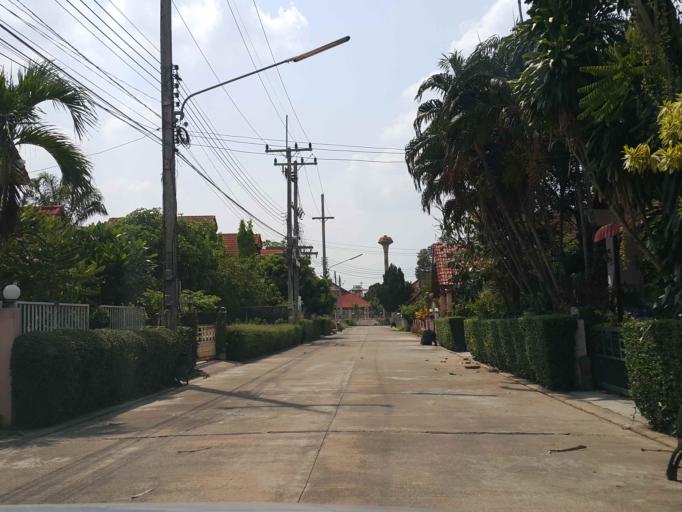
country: TH
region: Chiang Mai
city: Hang Dong
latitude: 18.7071
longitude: 98.9484
